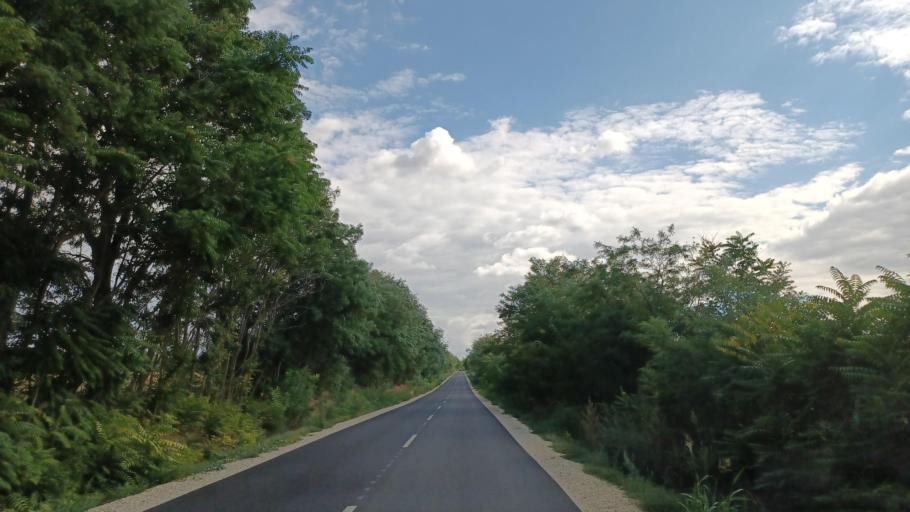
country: HU
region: Tolna
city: Nagydorog
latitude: 46.6056
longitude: 18.6927
